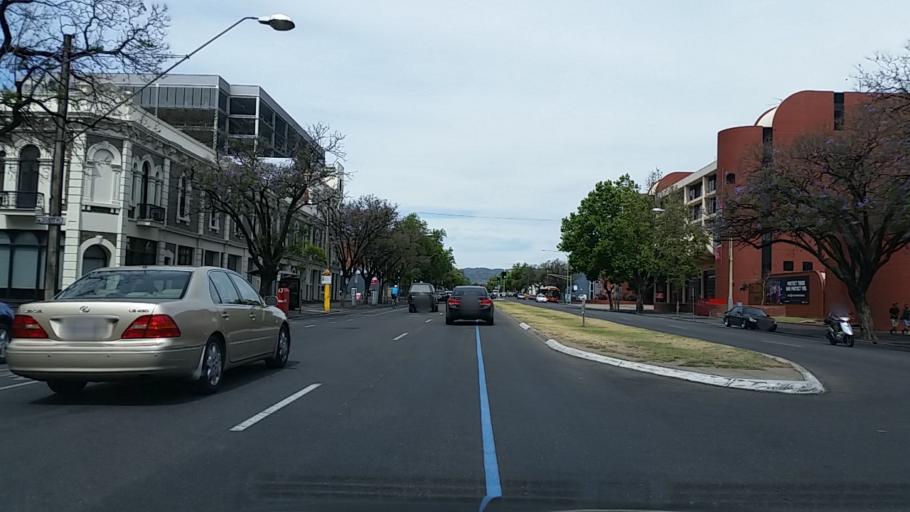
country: AU
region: South Australia
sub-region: Adelaide
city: Adelaide
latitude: -34.9284
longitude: 138.6034
